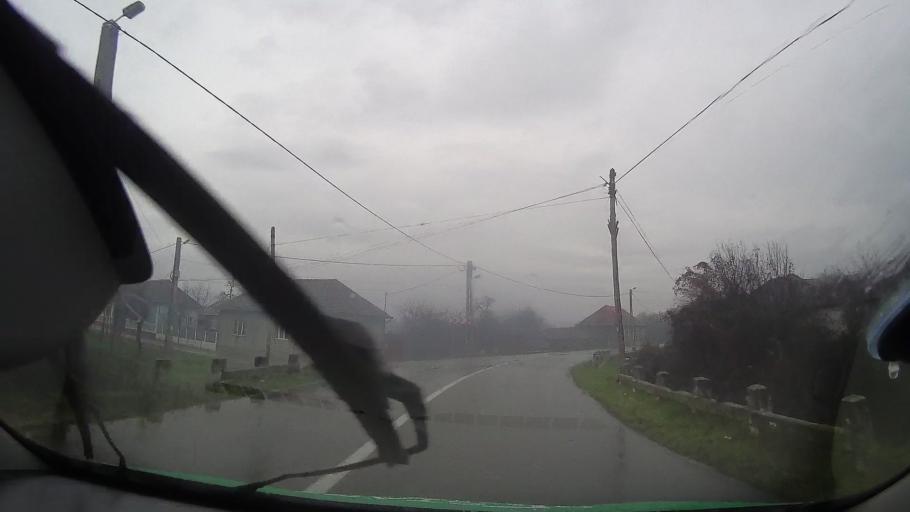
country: RO
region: Bihor
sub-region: Comuna Holod
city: Vintere
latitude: 46.7703
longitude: 22.1384
